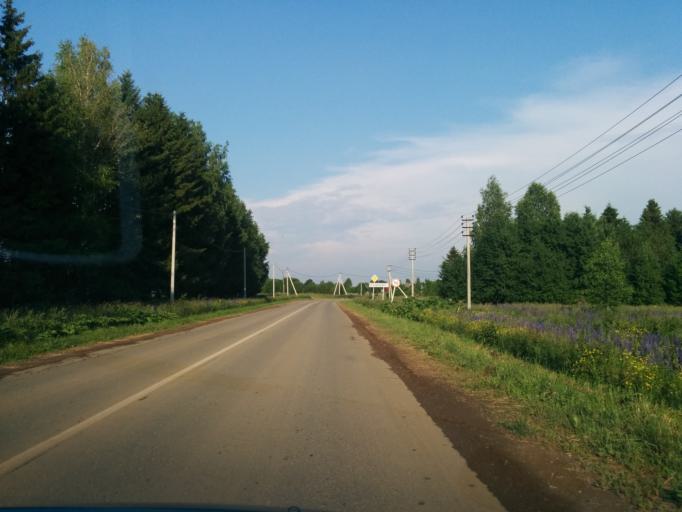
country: RU
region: Perm
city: Polazna
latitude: 58.2373
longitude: 56.2836
